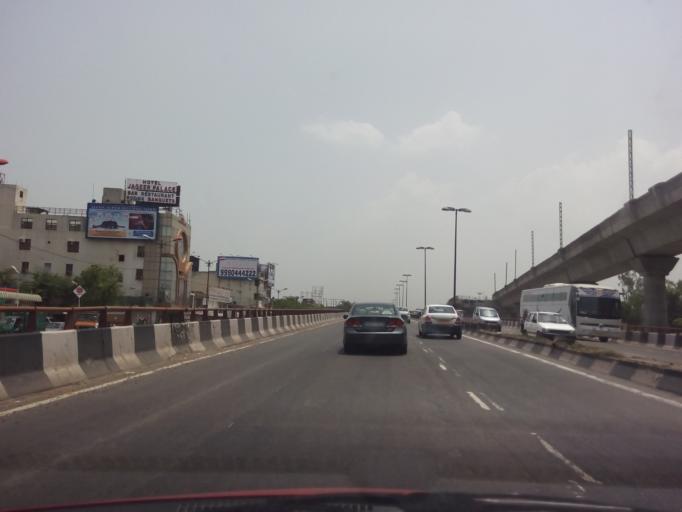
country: IN
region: NCT
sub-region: North West Delhi
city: Pitampura
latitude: 28.6395
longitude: 77.1293
